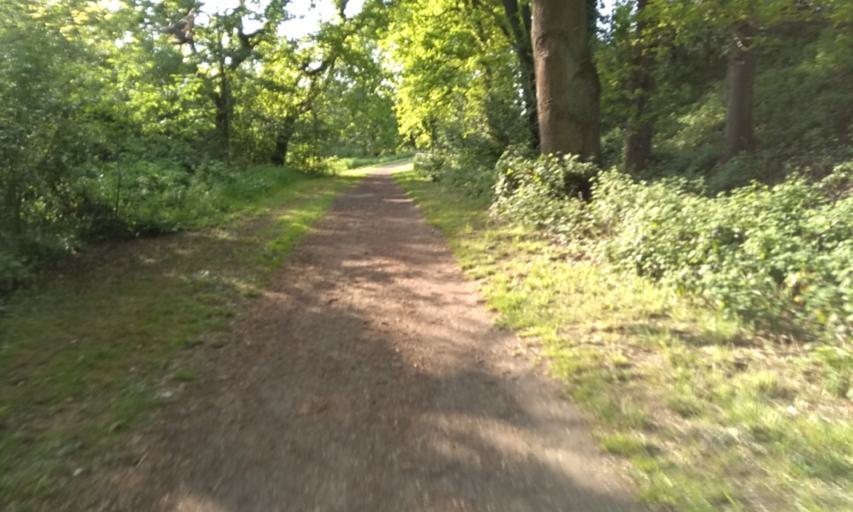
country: DE
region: Lower Saxony
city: Horneburg
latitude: 53.5048
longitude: 9.5809
